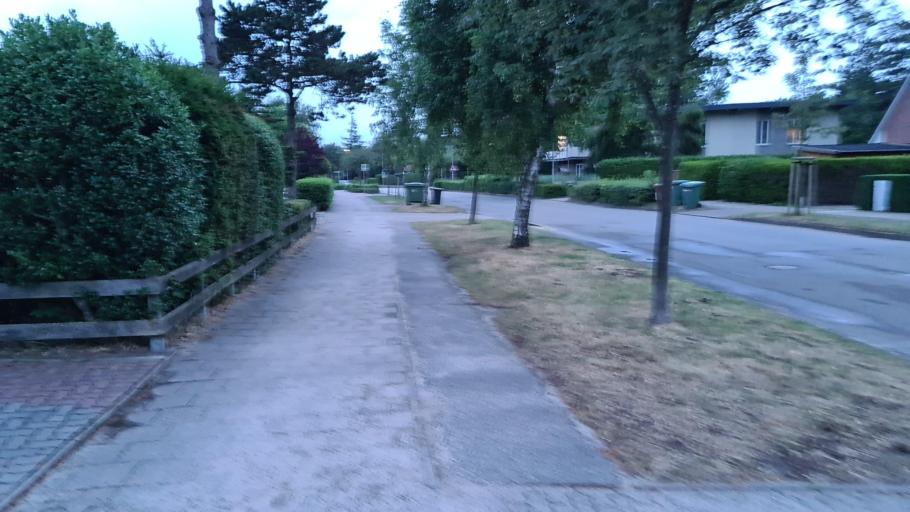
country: DE
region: Schleswig-Holstein
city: Sankt Peter-Ording
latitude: 54.2997
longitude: 8.6423
